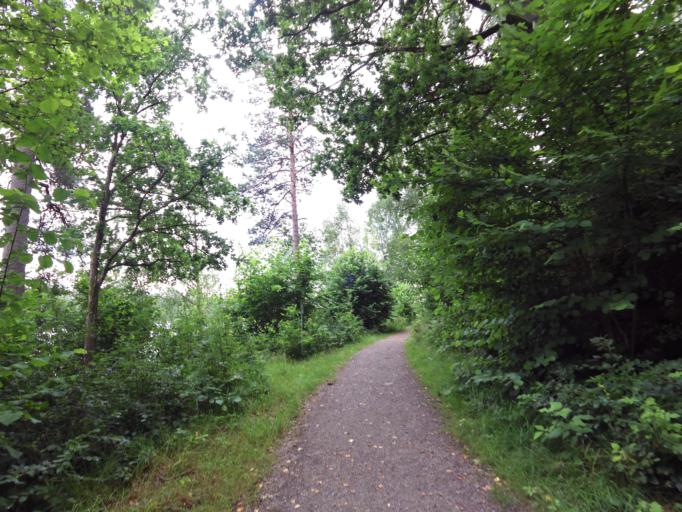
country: SE
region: Blekinge
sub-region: Olofstroms Kommun
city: Olofstroem
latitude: 56.3508
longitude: 14.5923
